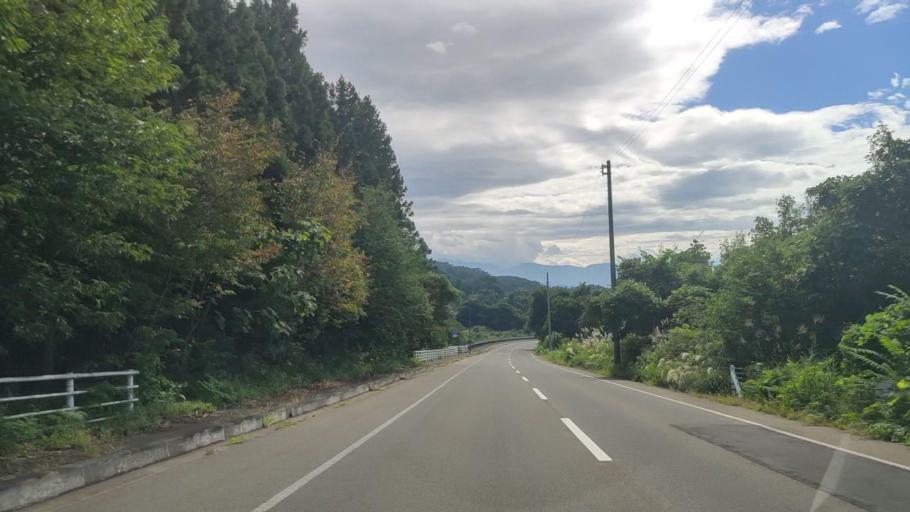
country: JP
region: Nagano
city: Nakano
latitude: 36.7921
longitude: 138.3164
